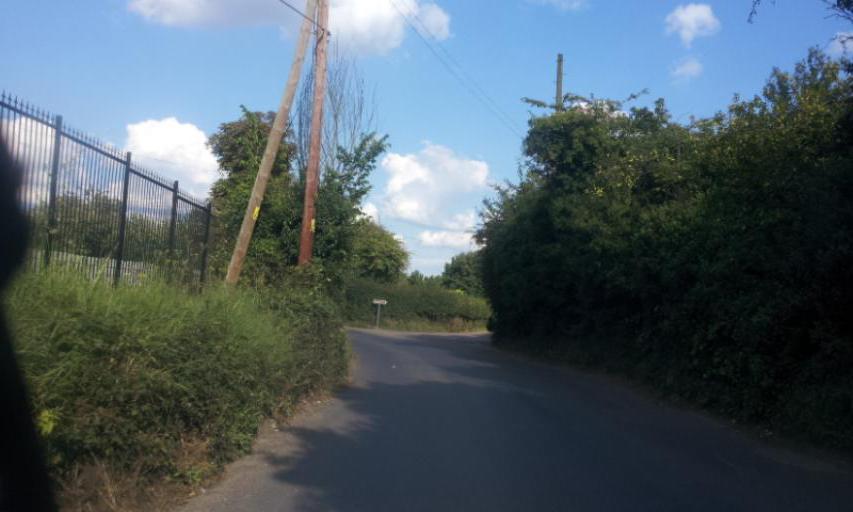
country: GB
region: England
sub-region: Kent
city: Swanley
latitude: 51.4064
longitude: 0.1685
